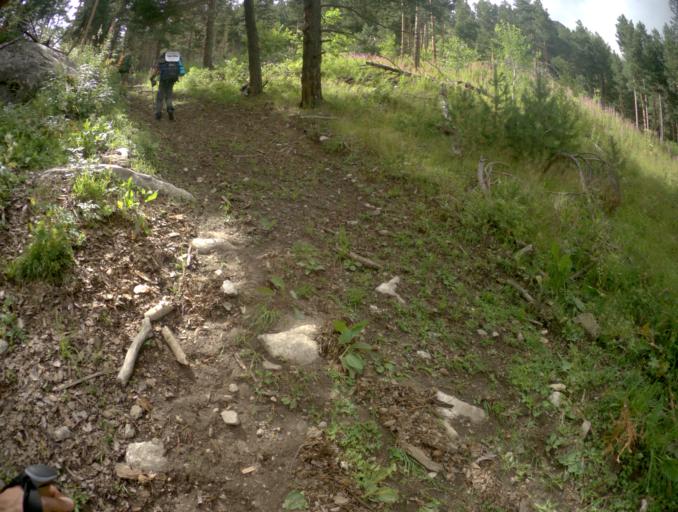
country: RU
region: Karachayevo-Cherkesiya
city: Uchkulan
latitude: 43.3458
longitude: 42.1510
